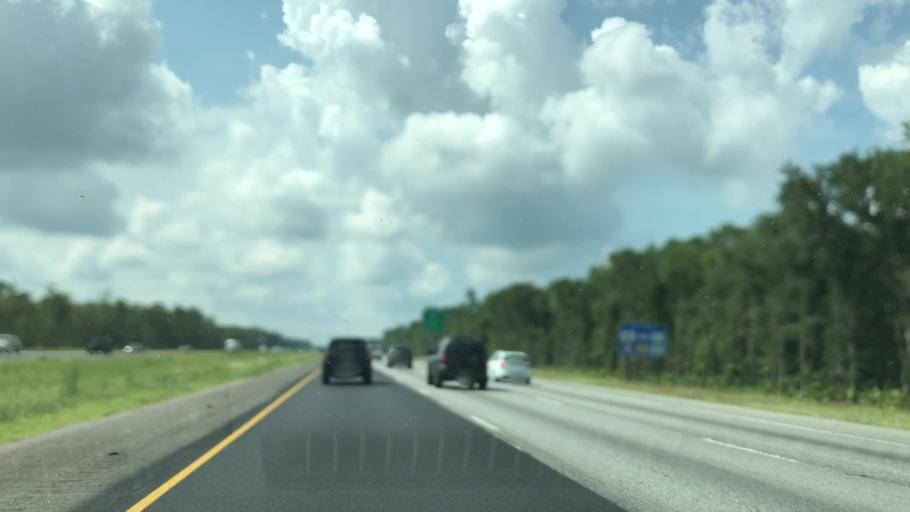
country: US
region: Georgia
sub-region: Camden County
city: Kingsland
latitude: 30.8122
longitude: -81.6641
